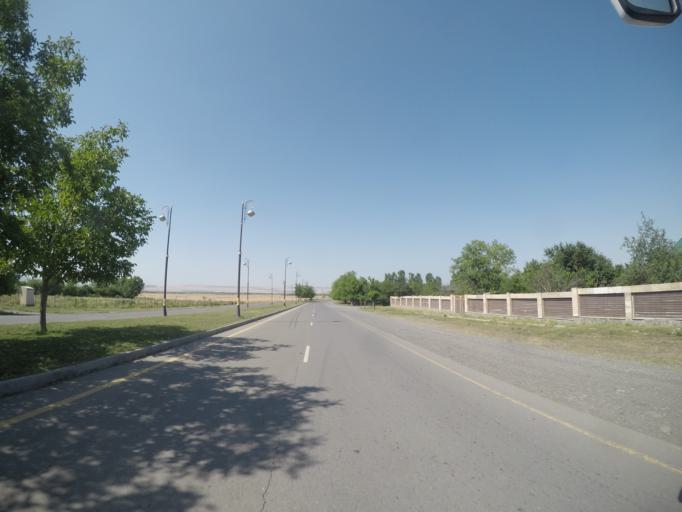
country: AZ
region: Qabala Rayon
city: Qutqashen
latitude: 40.8573
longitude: 47.7533
